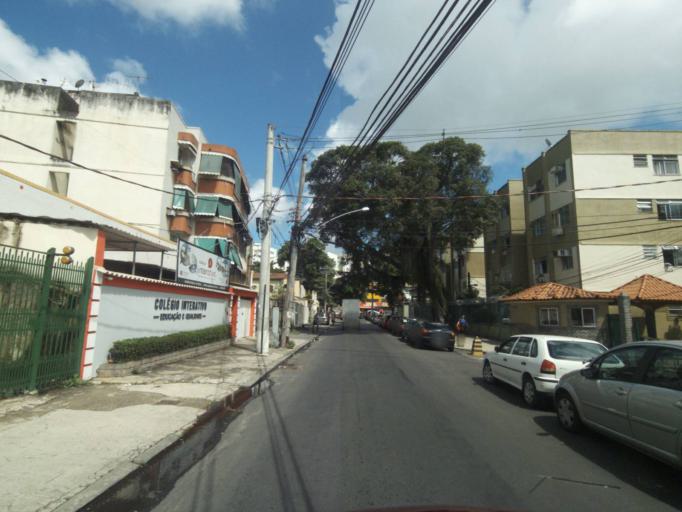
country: BR
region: Rio de Janeiro
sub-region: Sao Joao De Meriti
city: Sao Joao de Meriti
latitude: -22.9275
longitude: -43.3563
